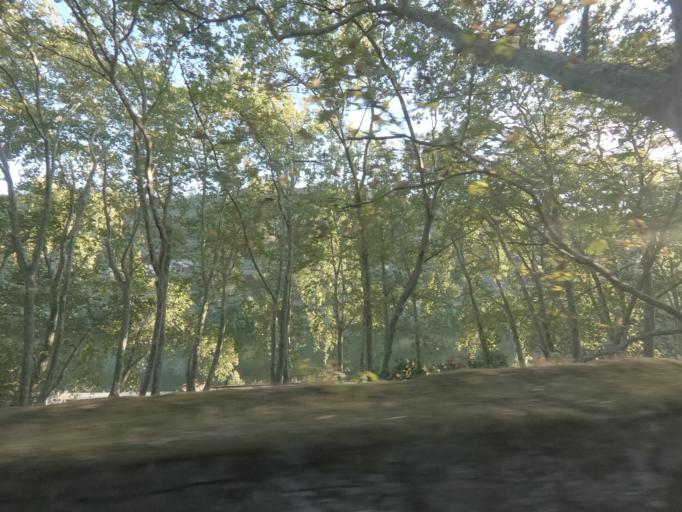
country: PT
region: Vila Real
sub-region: Mesao Frio
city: Mesao Frio
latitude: 41.1552
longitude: -7.8375
